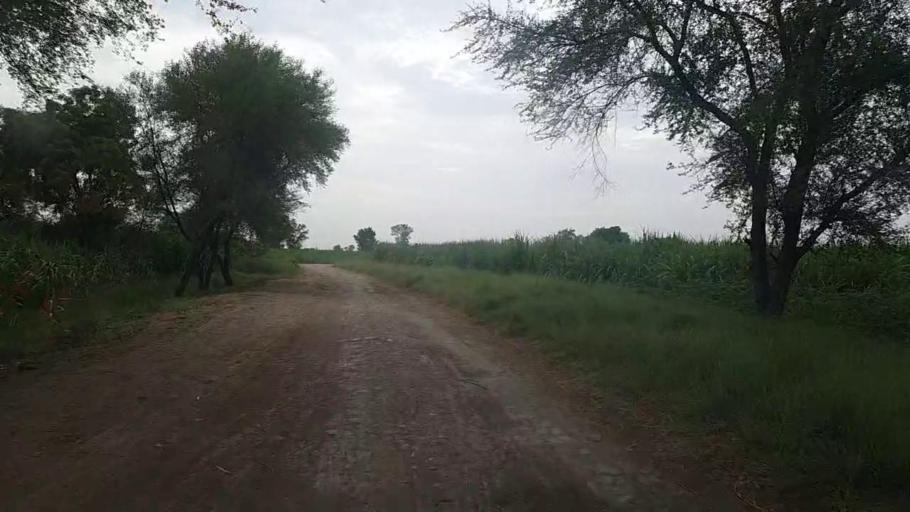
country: PK
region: Sindh
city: Karaundi
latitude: 26.9579
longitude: 68.3495
